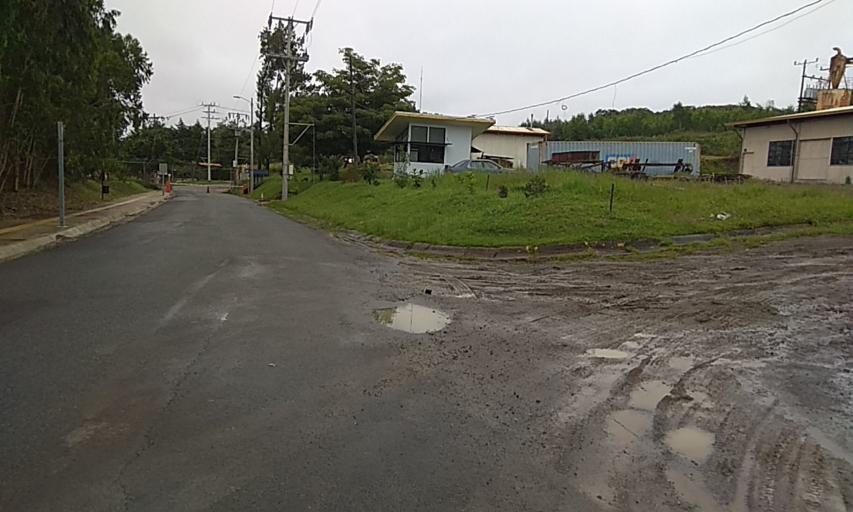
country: CR
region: Cartago
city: Cartago
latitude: 9.8495
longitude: -83.9110
